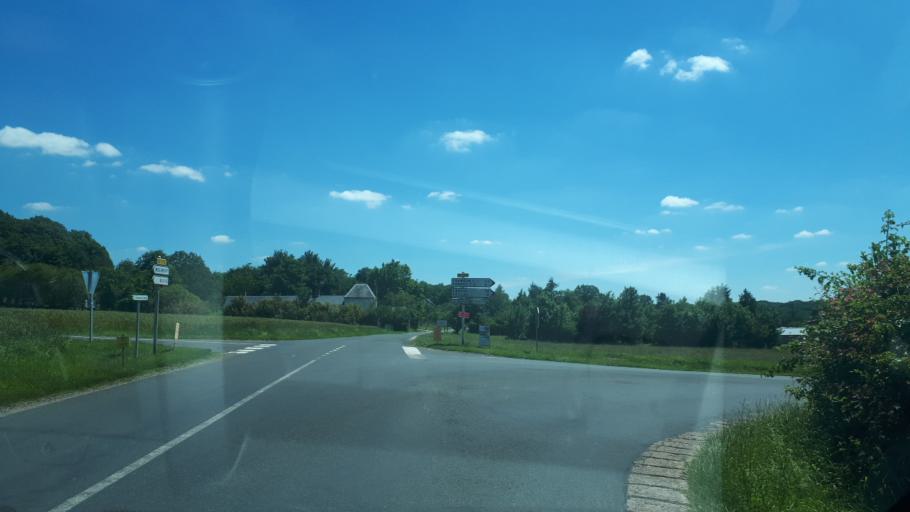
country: FR
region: Centre
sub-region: Departement du Loir-et-Cher
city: Chouzy-sur-Cisse
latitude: 47.5653
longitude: 1.2166
